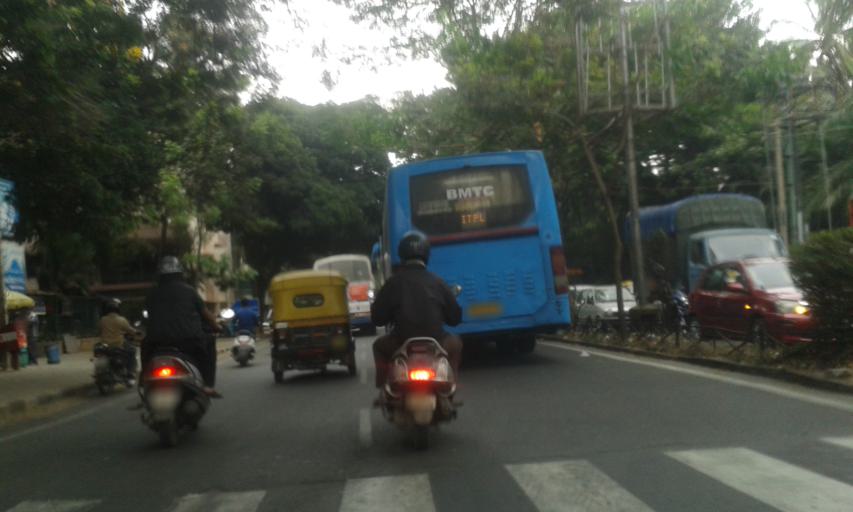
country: IN
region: Karnataka
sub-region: Bangalore Urban
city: Bangalore
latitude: 12.9172
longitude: 77.5804
